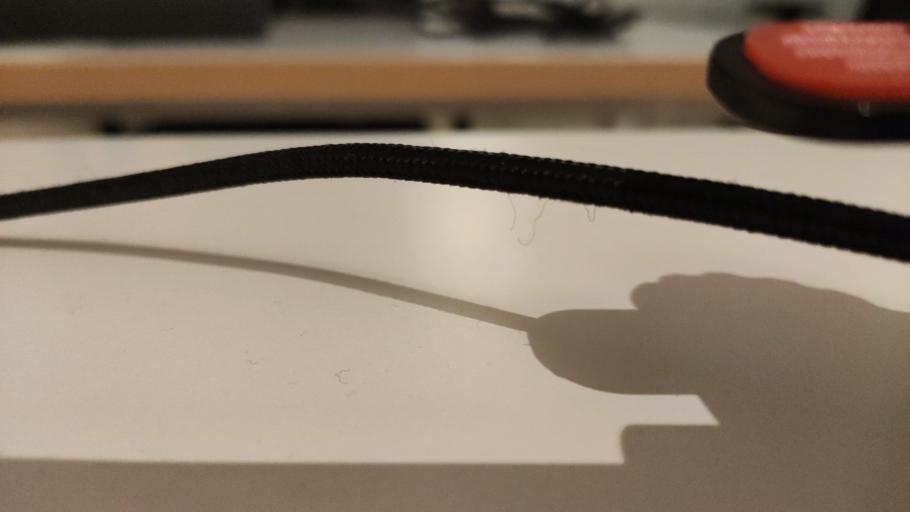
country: RU
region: Moskovskaya
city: Kurovskoye
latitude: 55.5469
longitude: 38.8734
